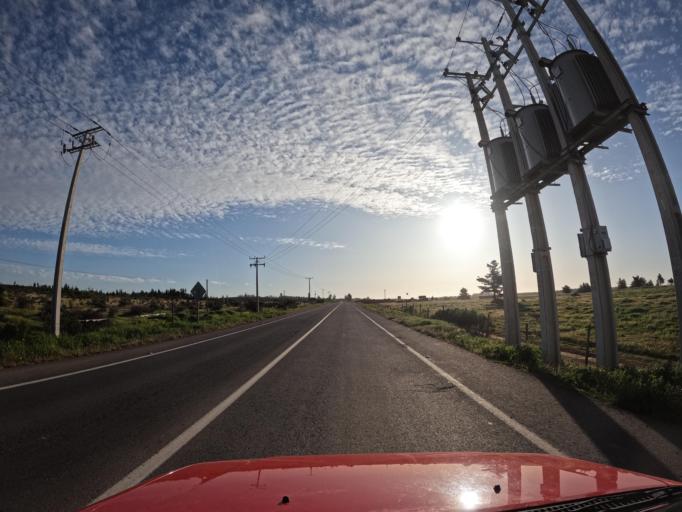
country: CL
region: Valparaiso
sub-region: San Antonio Province
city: San Antonio
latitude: -34.0730
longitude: -71.6330
